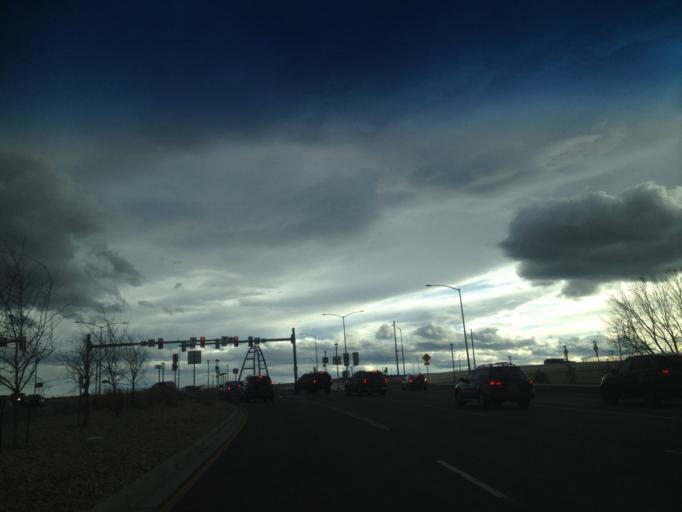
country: US
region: Colorado
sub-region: Boulder County
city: Superior
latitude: 39.9596
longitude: -105.1654
